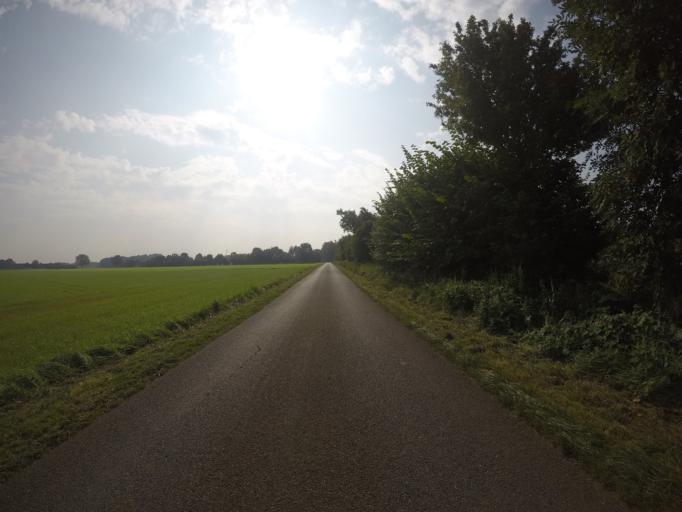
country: DE
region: North Rhine-Westphalia
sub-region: Regierungsbezirk Dusseldorf
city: Mehrhoog
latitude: 51.8047
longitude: 6.5466
